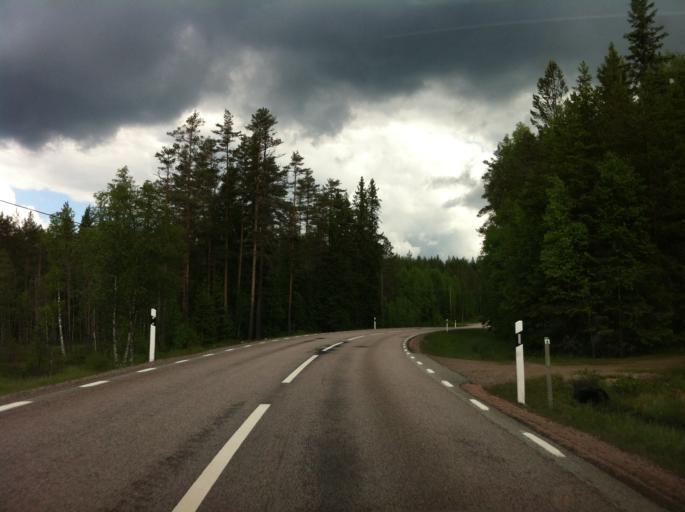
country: SE
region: Vaermland
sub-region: Torsby Kommun
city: Torsby
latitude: 60.3094
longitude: 13.0952
